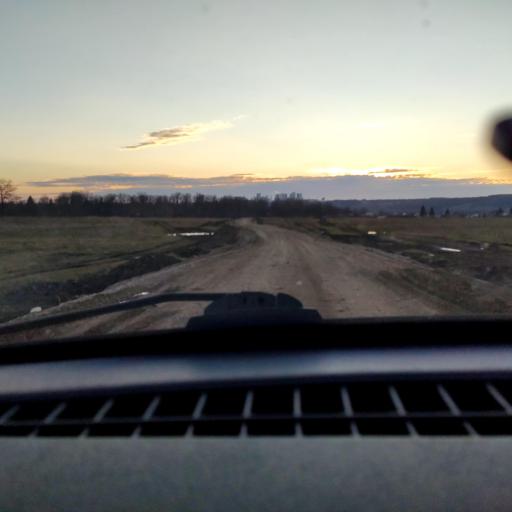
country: RU
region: Bashkortostan
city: Ufa
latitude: 54.7413
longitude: 56.0664
